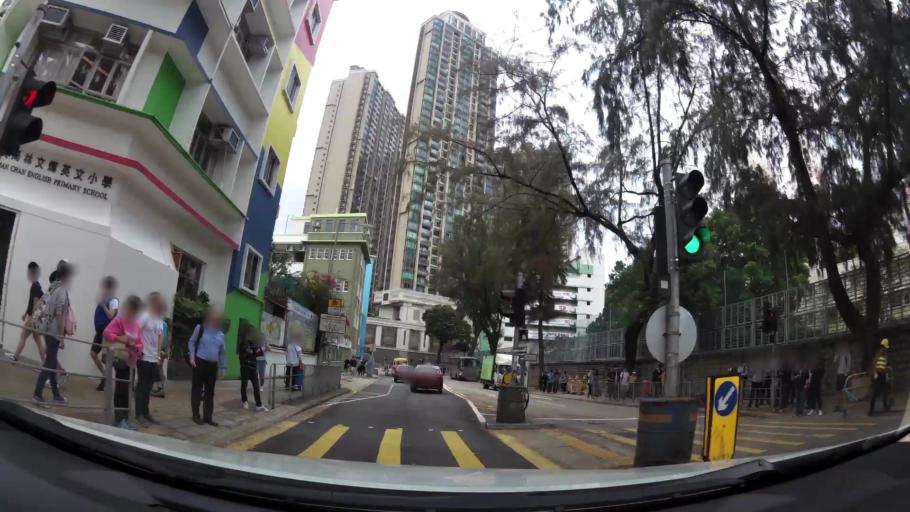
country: HK
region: Kowloon City
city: Kowloon
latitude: 22.3210
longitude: 114.1851
